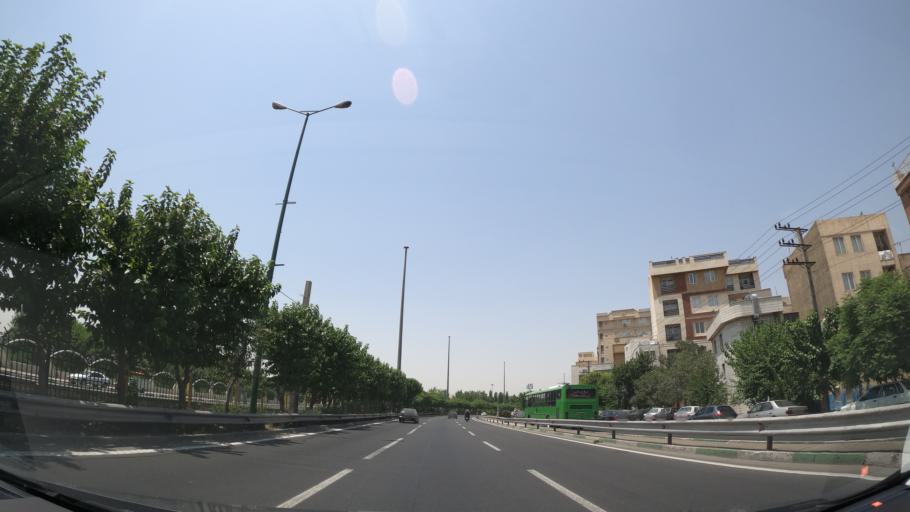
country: IR
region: Tehran
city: Tehran
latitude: 35.6527
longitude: 51.3847
